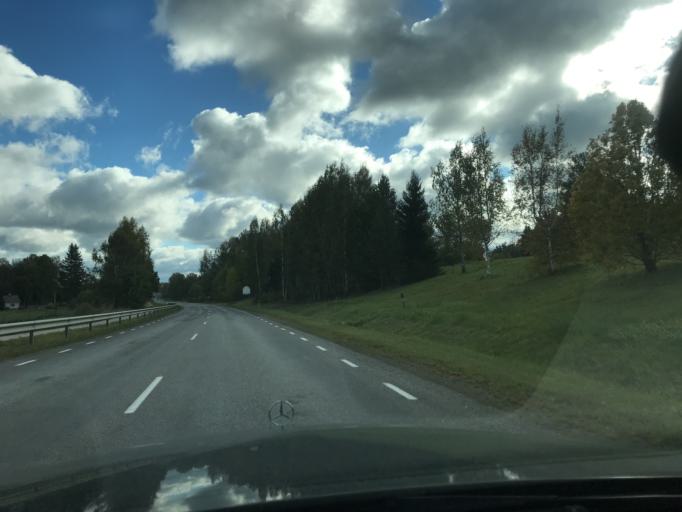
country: EE
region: Vorumaa
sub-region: Antsla vald
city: Vana-Antsla
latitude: 57.9284
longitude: 26.3248
